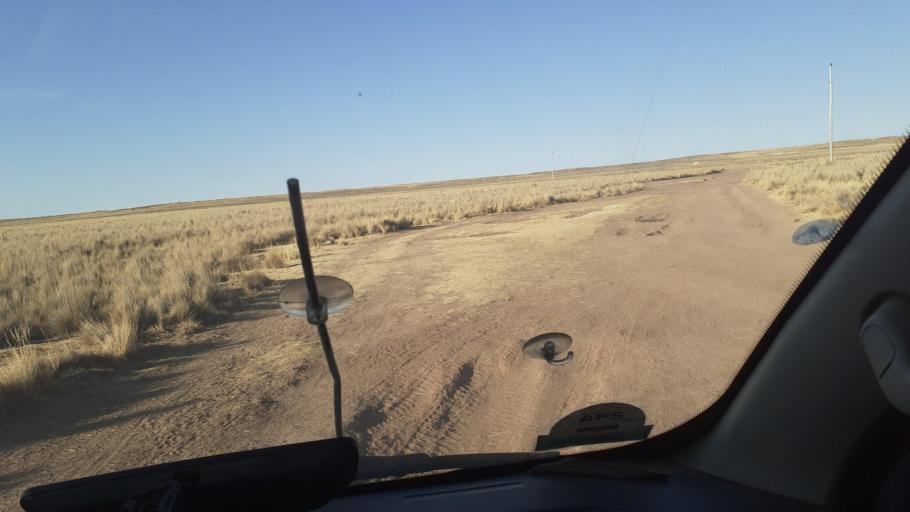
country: BO
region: La Paz
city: Tiahuanaco
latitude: -16.9985
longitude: -68.7254
